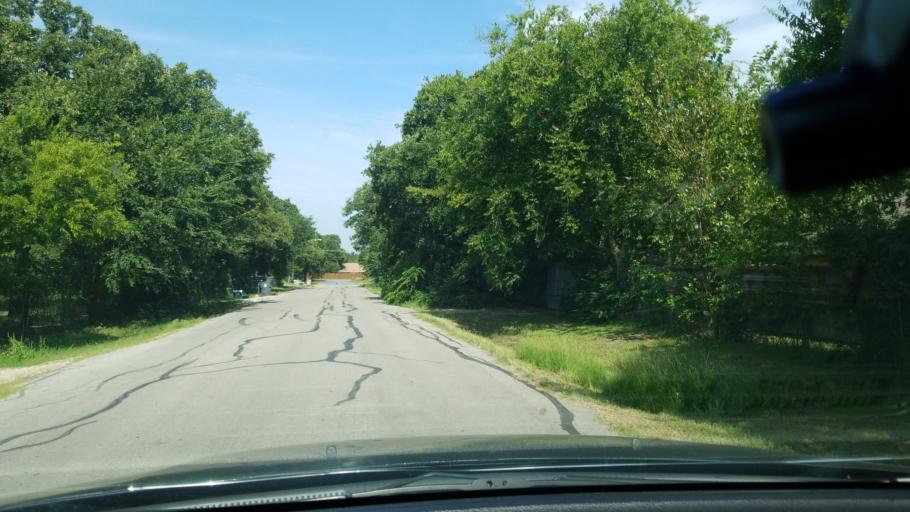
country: US
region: Texas
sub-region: Dallas County
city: Balch Springs
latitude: 32.7305
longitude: -96.6372
